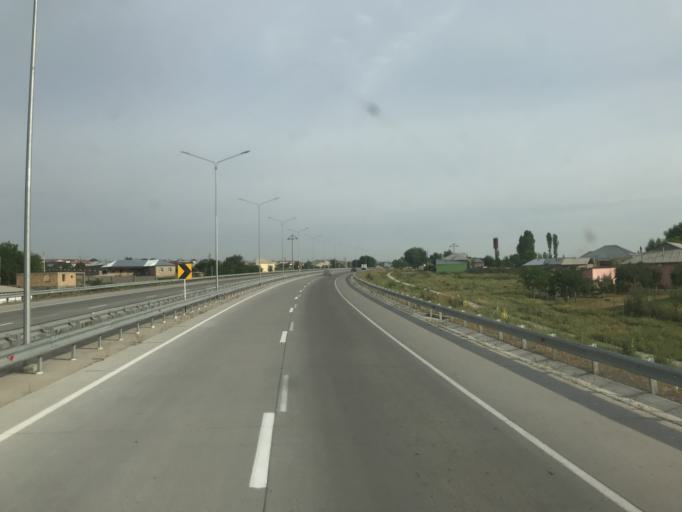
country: KZ
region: Ongtustik Qazaqstan
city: Qazyqurt
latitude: 41.7868
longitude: 69.3947
